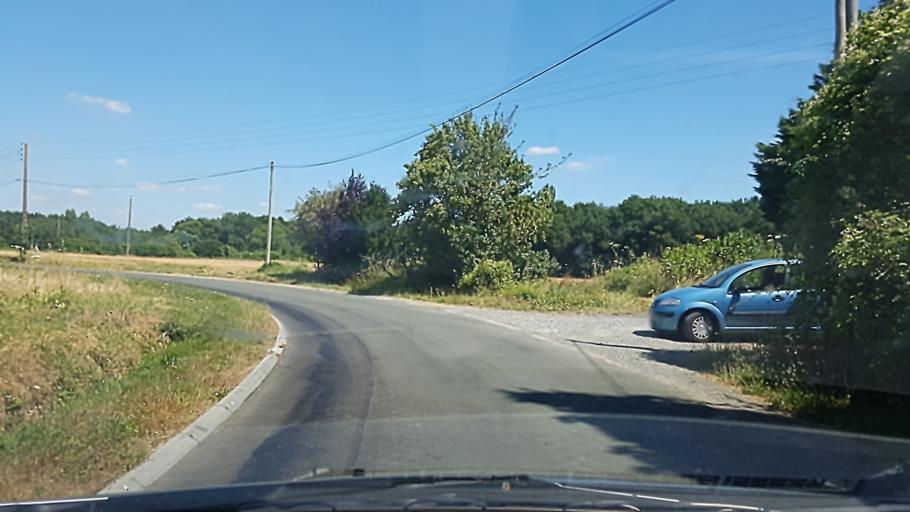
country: FR
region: Pays de la Loire
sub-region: Departement de Maine-et-Loire
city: Corze
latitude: 47.5337
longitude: -0.3830
